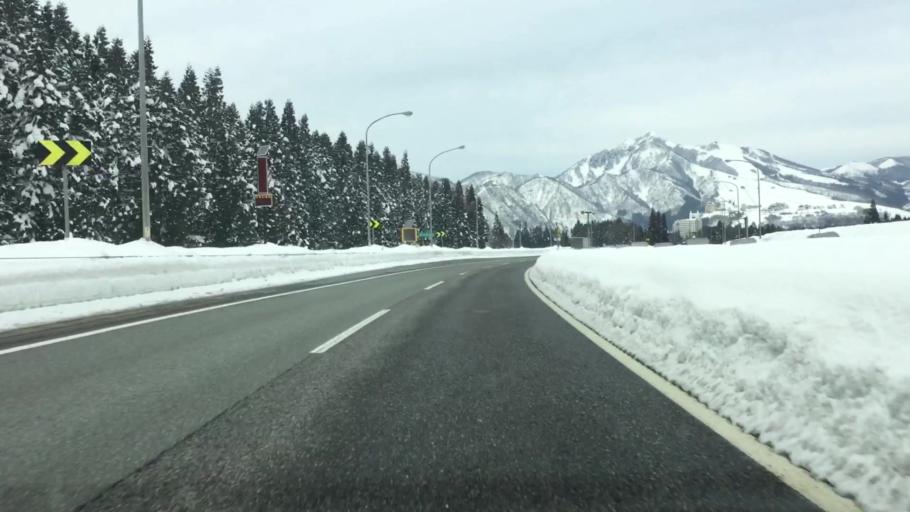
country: JP
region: Niigata
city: Shiozawa
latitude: 36.8936
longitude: 138.8456
